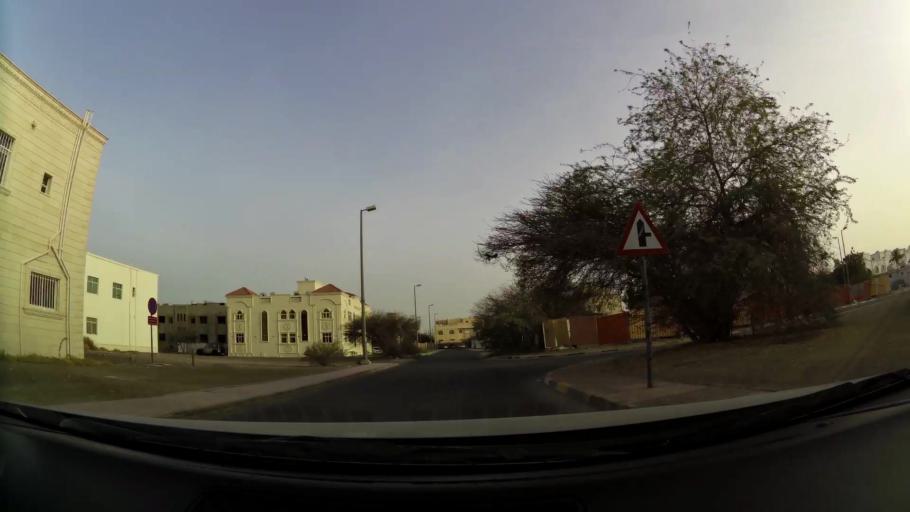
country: OM
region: Al Buraimi
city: Al Buraymi
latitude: 24.2463
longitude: 55.7343
